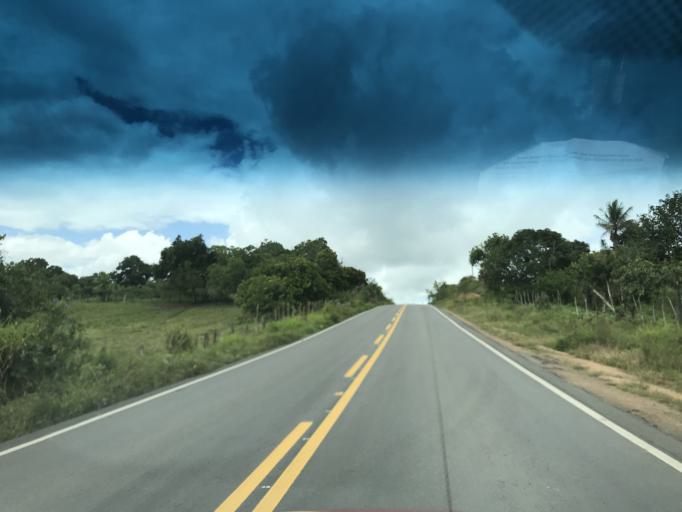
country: BR
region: Bahia
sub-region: Conceicao Do Almeida
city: Conceicao do Almeida
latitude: -12.6910
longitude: -39.2471
